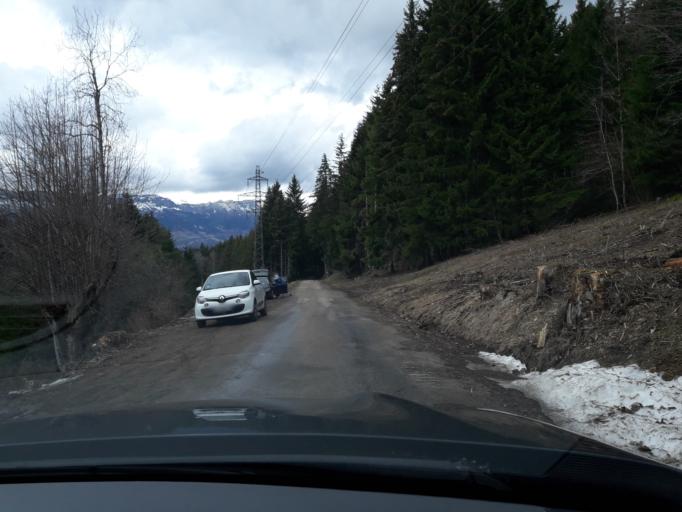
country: FR
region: Rhone-Alpes
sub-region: Departement de l'Isere
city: Le Champ-pres-Froges
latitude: 45.2428
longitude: 5.9800
